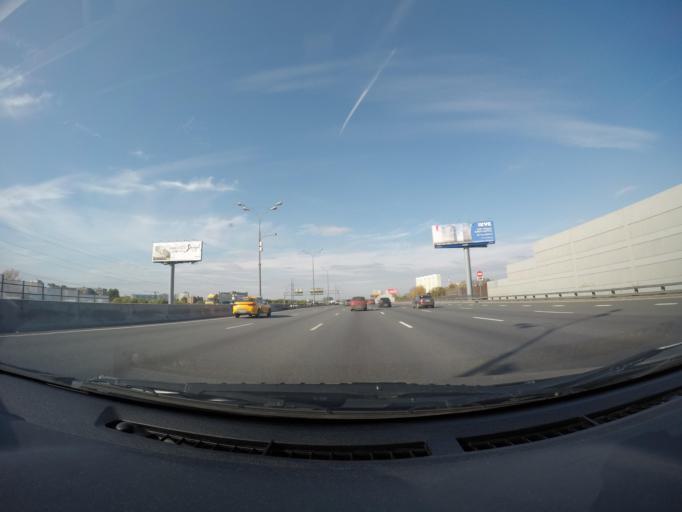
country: RU
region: Moscow
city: Yaroslavskiy
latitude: 55.8851
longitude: 37.7206
